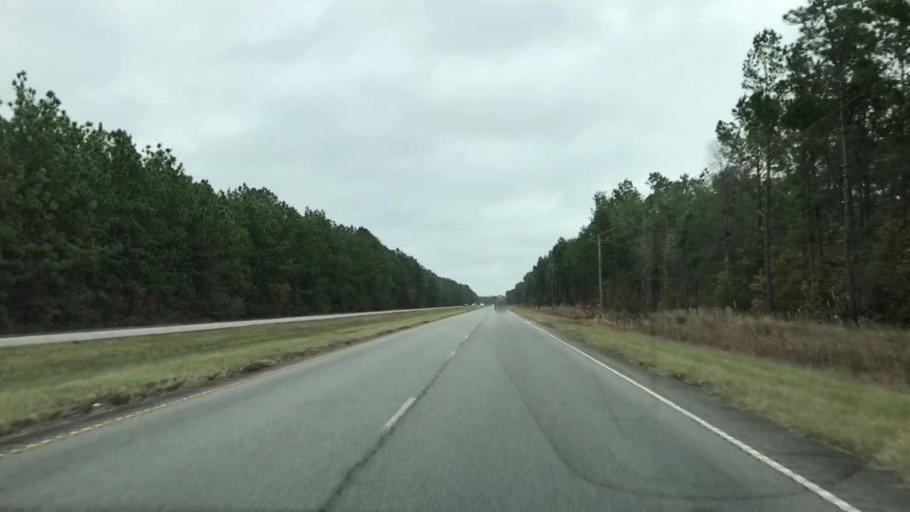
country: US
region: South Carolina
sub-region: Charleston County
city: Awendaw
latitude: 33.0144
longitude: -79.6359
